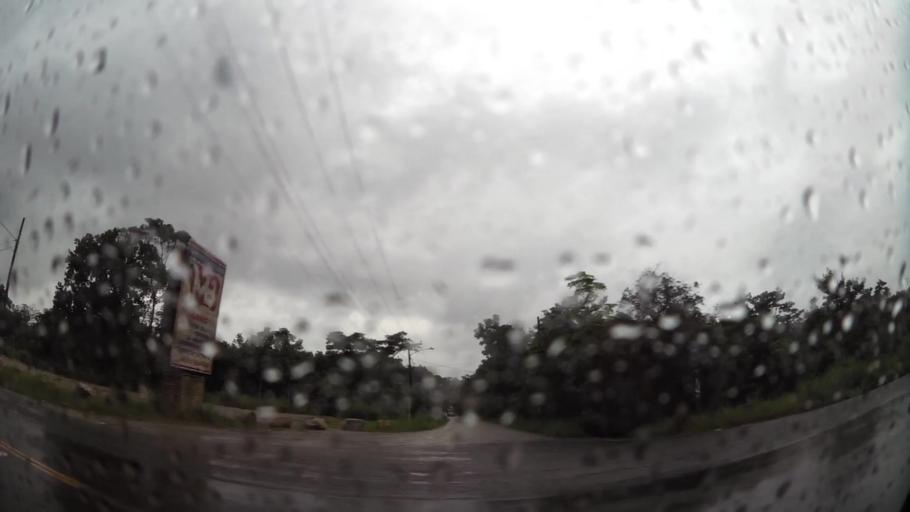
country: PA
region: Colon
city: Quebrada Bonita Adentro
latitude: 9.2853
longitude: -79.7156
